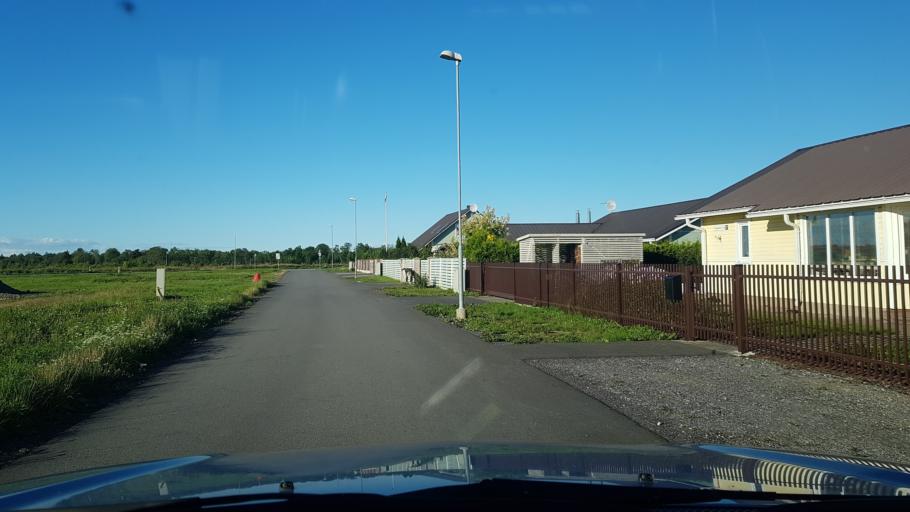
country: EE
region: Harju
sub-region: Rae vald
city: Jueri
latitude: 59.3857
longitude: 24.8469
